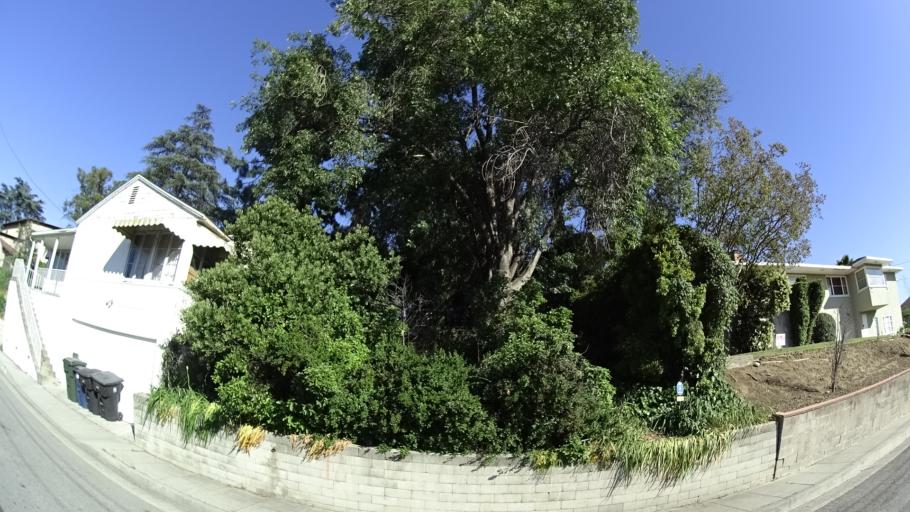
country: US
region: California
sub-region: Los Angeles County
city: Belvedere
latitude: 34.0731
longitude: -118.1590
